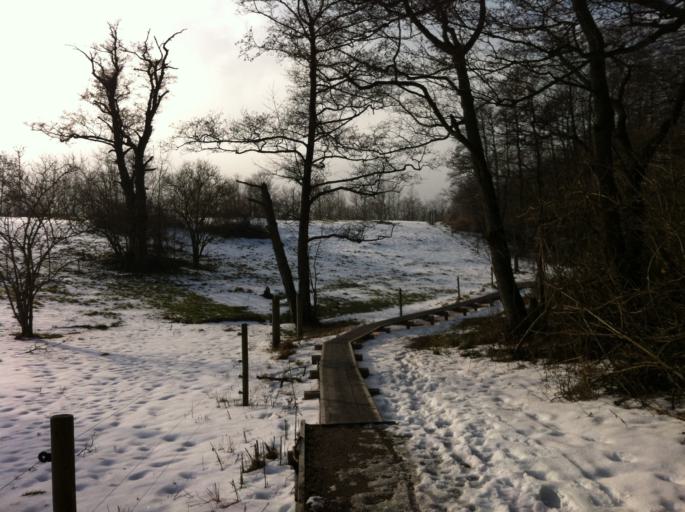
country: SE
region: Skane
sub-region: Helsingborg
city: Gantofta
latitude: 55.9994
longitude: 12.7720
